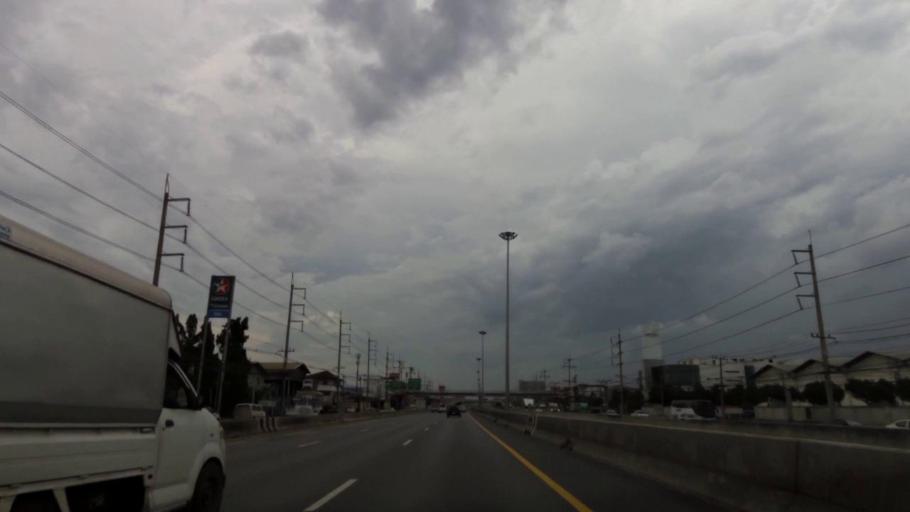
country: TH
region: Pathum Thani
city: Khlong Luang
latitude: 14.1012
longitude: 100.6188
